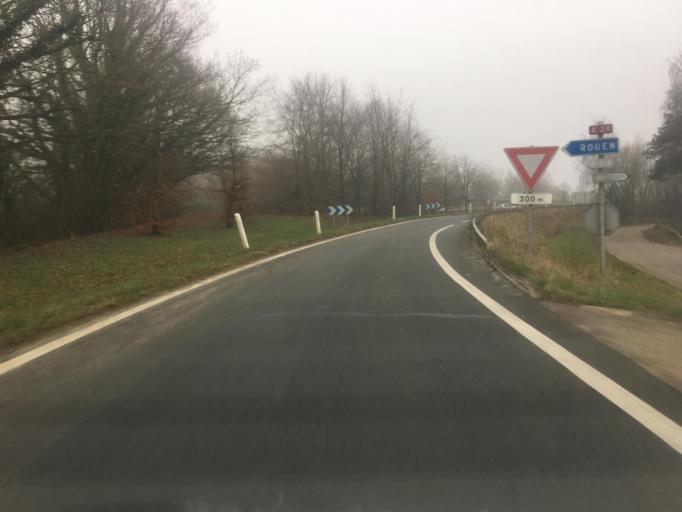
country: FR
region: Haute-Normandie
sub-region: Departement de la Seine-Maritime
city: Neufchatel-en-Bray
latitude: 49.7206
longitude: 1.4248
